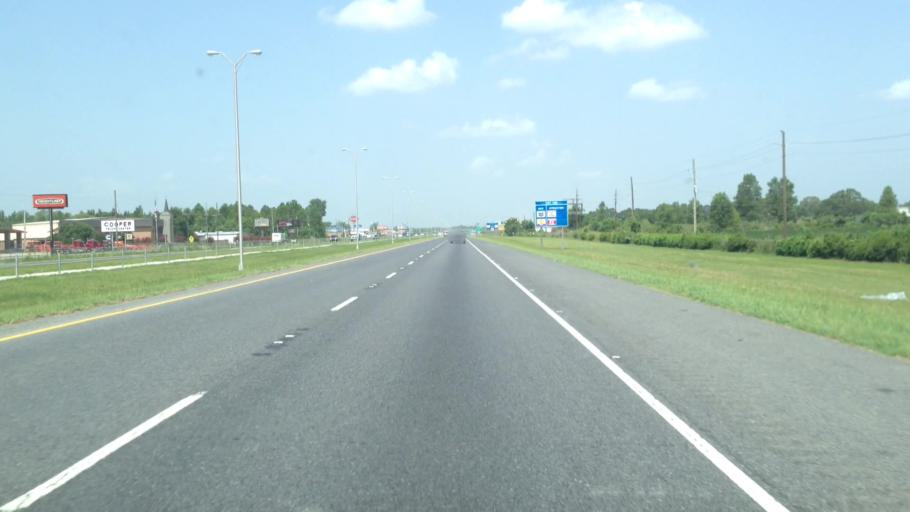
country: US
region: Louisiana
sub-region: Ouachita Parish
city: Lakeshore
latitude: 32.4929
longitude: -92.0346
